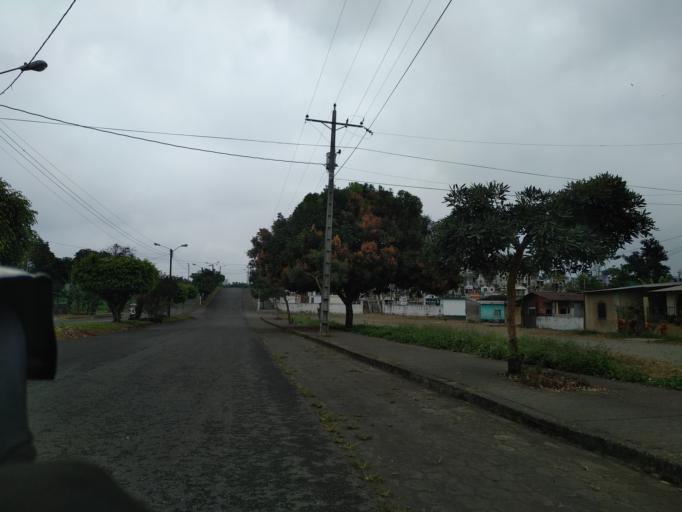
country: EC
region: Cotopaxi
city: La Mana
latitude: -0.9581
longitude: -79.3508
